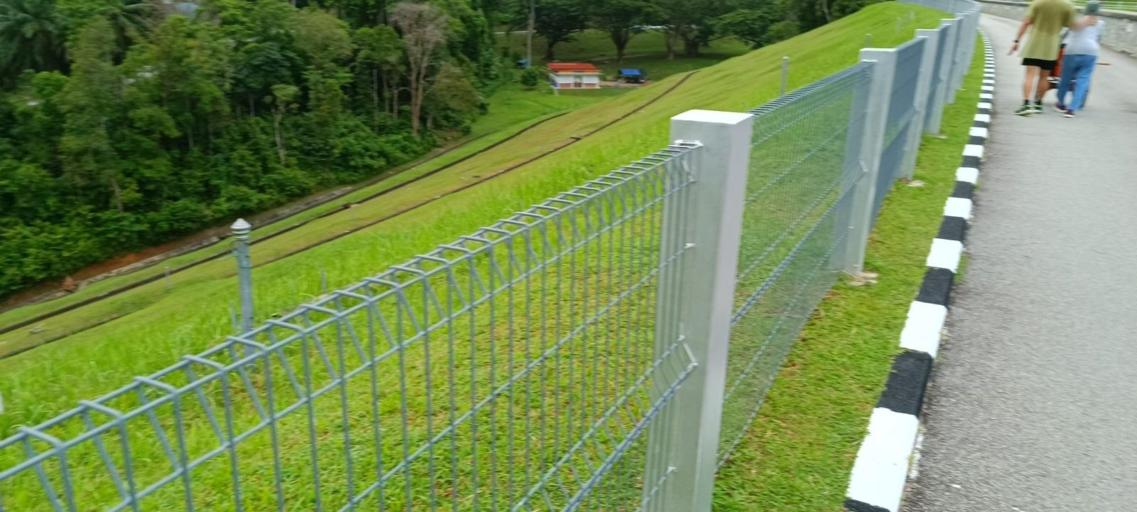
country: MY
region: Penang
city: Kampung Sungai Ara
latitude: 5.3962
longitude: 100.2633
